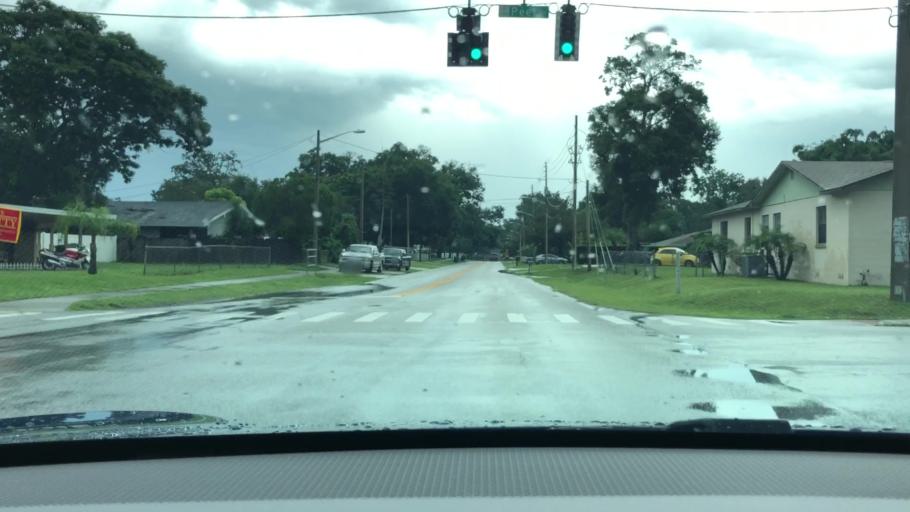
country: US
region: Florida
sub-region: Orange County
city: Conway
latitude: 28.5132
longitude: -81.3475
